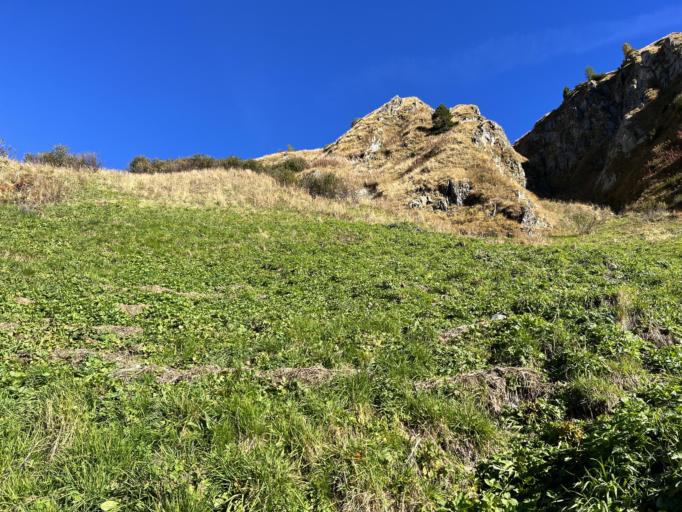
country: AT
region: Tyrol
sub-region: Politischer Bezirk Lienz
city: Untertilliach
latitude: 46.6379
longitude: 12.7180
